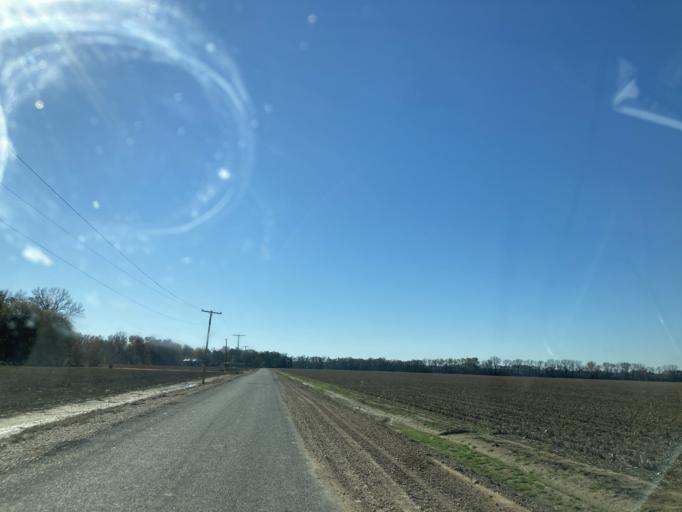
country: US
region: Mississippi
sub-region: Sharkey County
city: Rolling Fork
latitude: 32.8210
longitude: -90.7293
